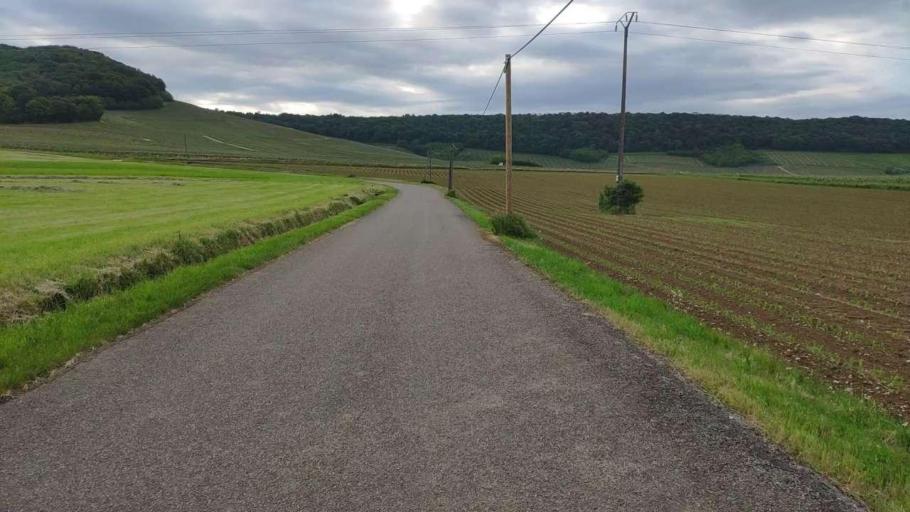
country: FR
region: Franche-Comte
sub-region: Departement du Jura
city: Perrigny
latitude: 46.7362
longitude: 5.5974
